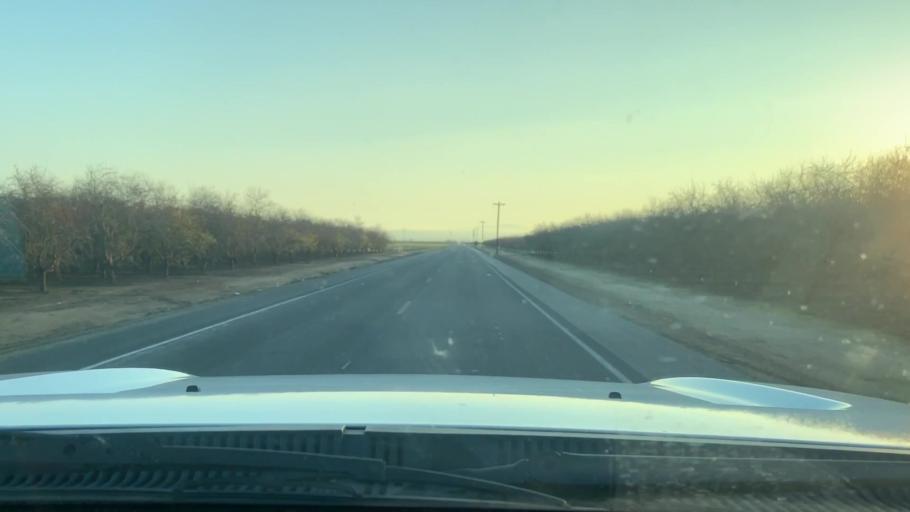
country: US
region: California
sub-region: Kern County
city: Wasco
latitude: 35.5002
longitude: -119.3919
